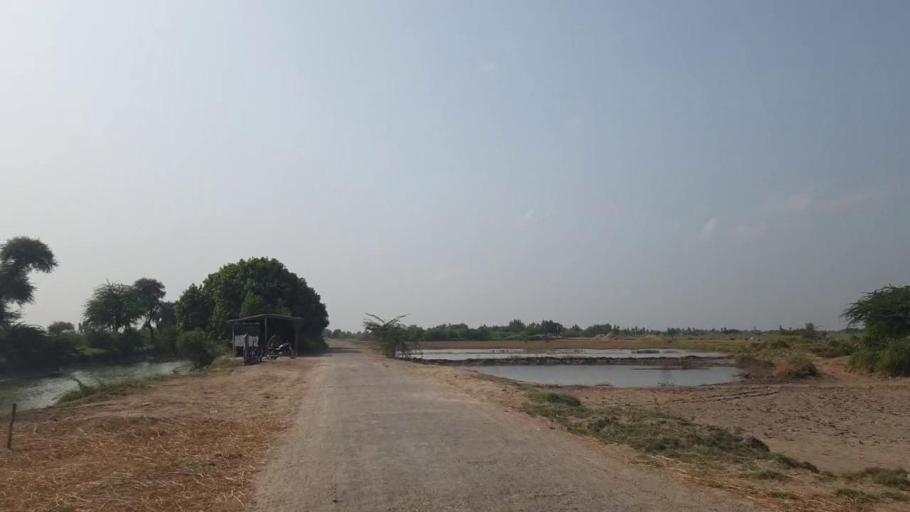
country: PK
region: Sindh
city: Talhar
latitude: 24.7728
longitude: 68.7720
